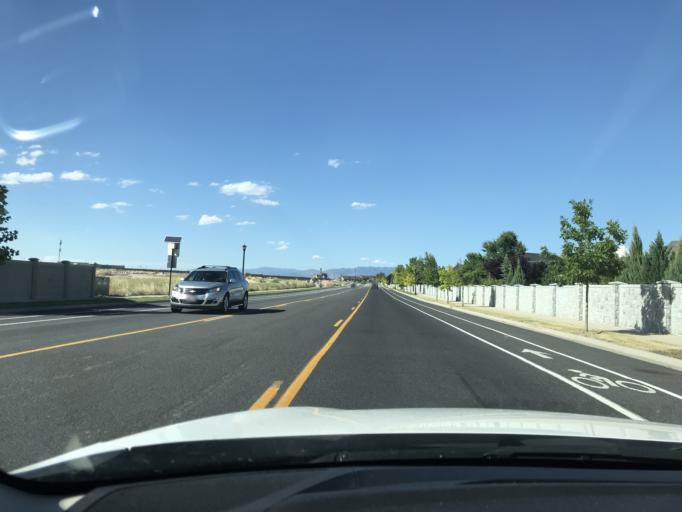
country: US
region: Utah
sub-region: Salt Lake County
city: South Jordan Heights
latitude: 40.5530
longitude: -111.9757
